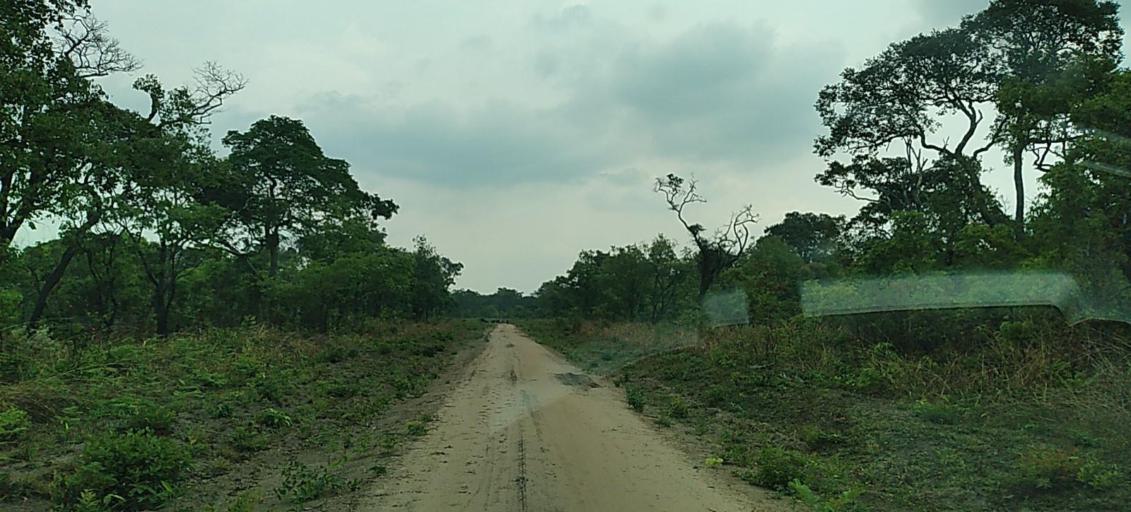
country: ZM
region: North-Western
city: Mwinilunga
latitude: -11.4071
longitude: 24.6242
